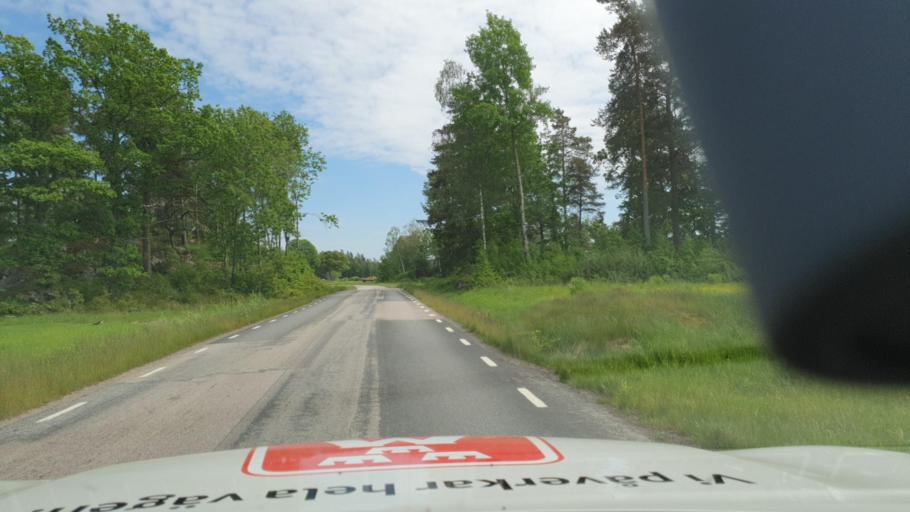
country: SE
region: Vaestra Goetaland
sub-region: Alingsas Kommun
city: Sollebrunn
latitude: 58.2140
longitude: 12.5280
